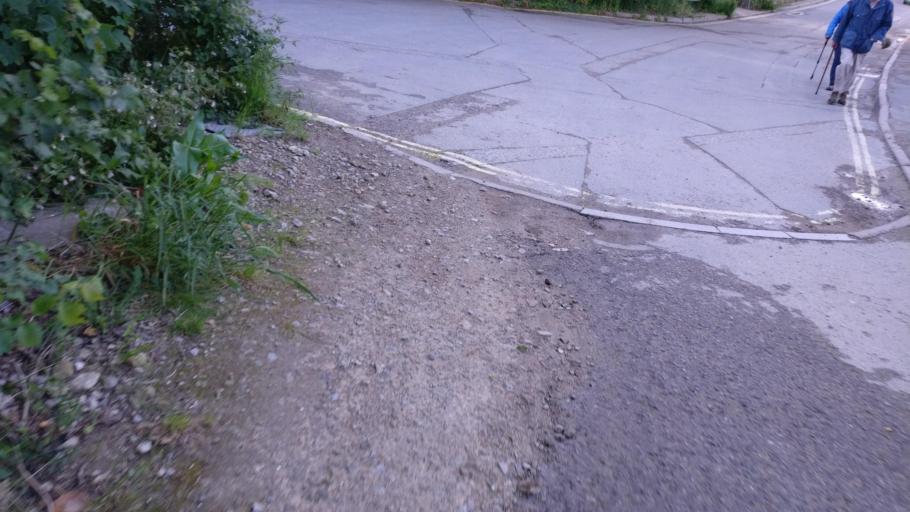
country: GB
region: England
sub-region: Dorset
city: Swanage
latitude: 50.6073
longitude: -2.0046
